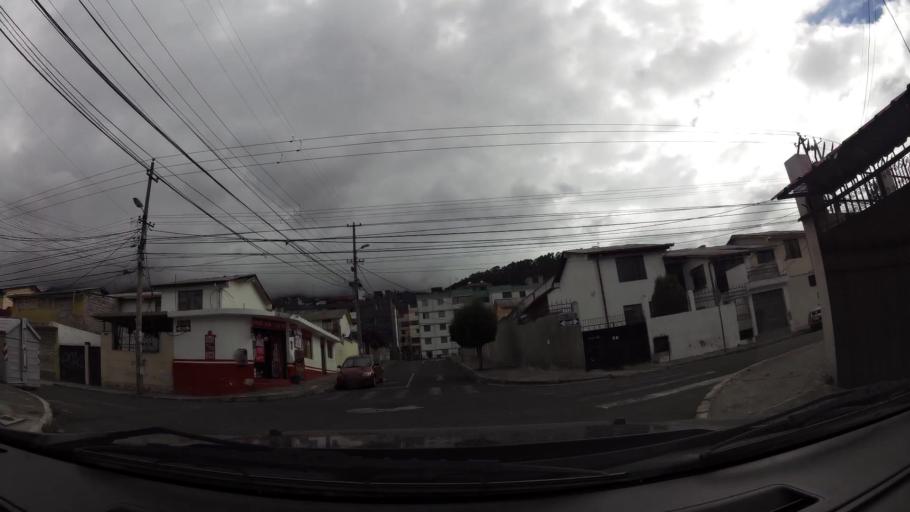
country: EC
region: Pichincha
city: Quito
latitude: -0.1302
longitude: -78.5007
